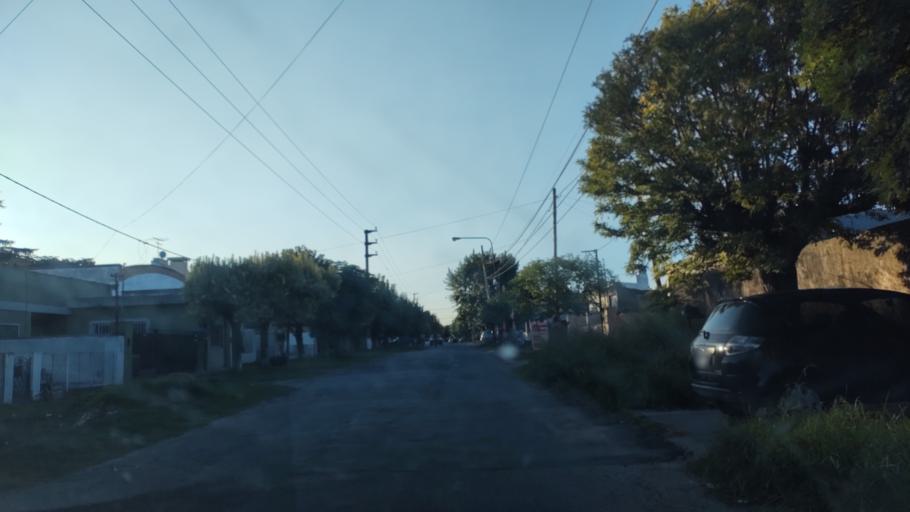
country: AR
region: Buenos Aires
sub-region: Partido de La Plata
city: La Plata
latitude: -34.9683
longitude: -57.9773
